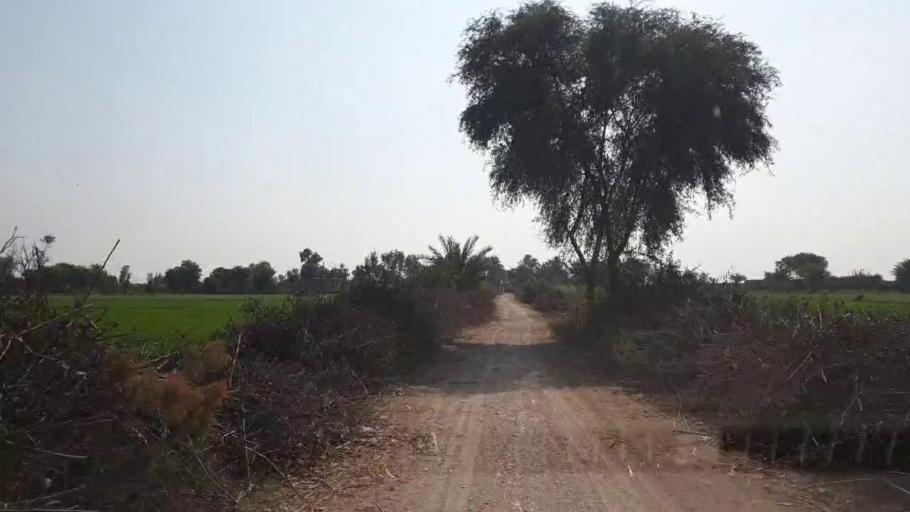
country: PK
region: Sindh
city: Shahdadpur
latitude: 25.9415
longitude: 68.4871
